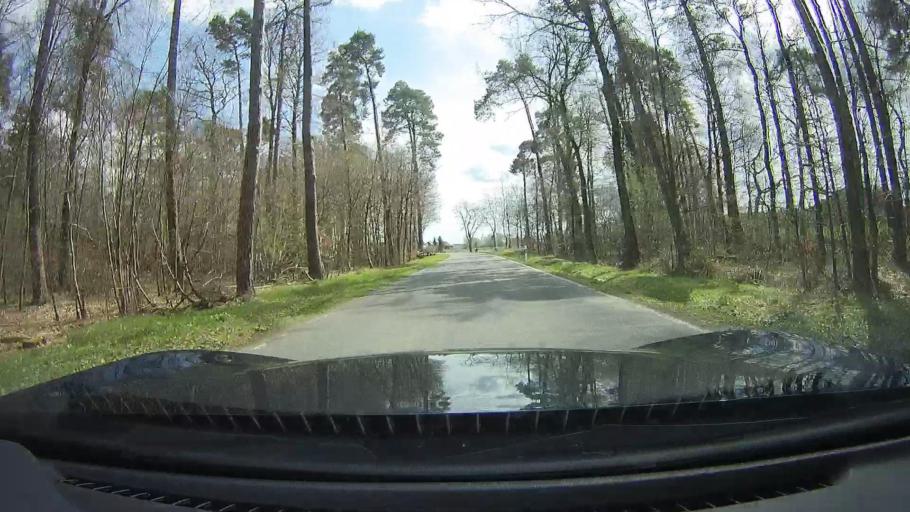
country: DE
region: Hesse
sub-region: Regierungsbezirk Darmstadt
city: Hesseneck
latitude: 49.6262
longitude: 9.1067
